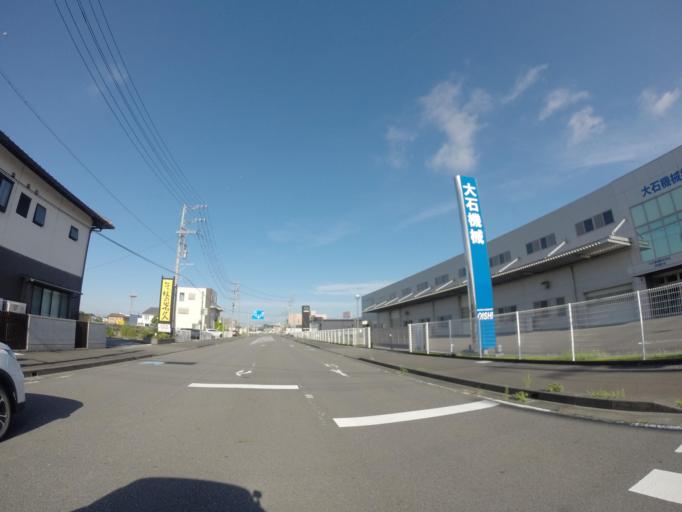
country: JP
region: Shizuoka
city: Yaizu
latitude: 34.8373
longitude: 138.3114
